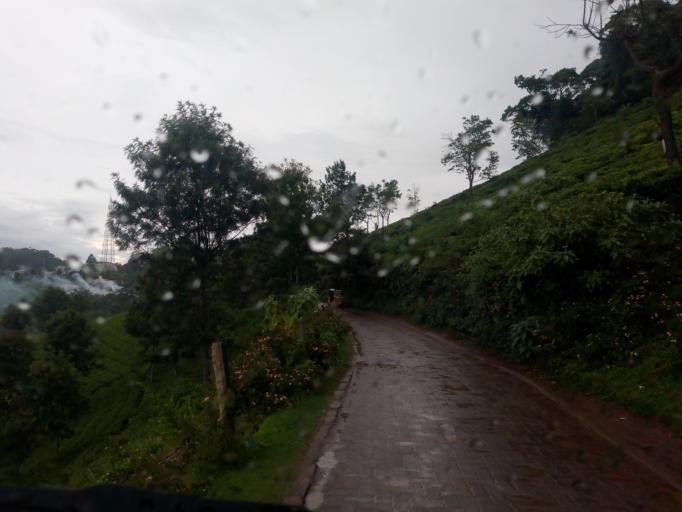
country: IN
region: Tamil Nadu
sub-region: Nilgiri
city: Wellington
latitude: 11.3488
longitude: 76.8153
